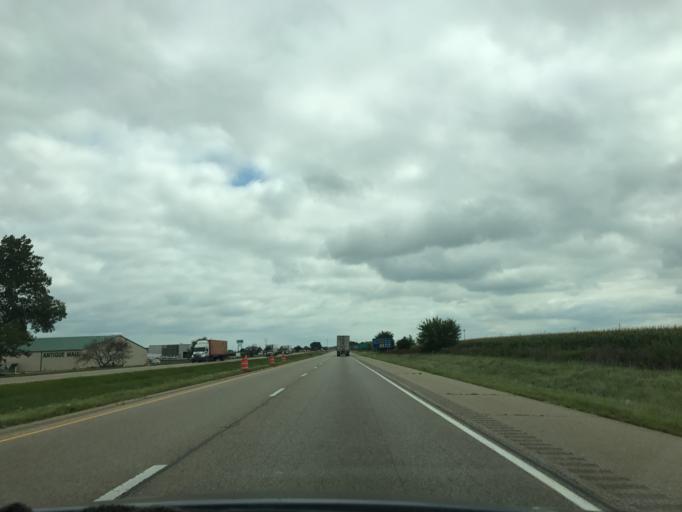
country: US
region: Illinois
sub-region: LaSalle County
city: Peru
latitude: 41.3649
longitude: -89.1429
